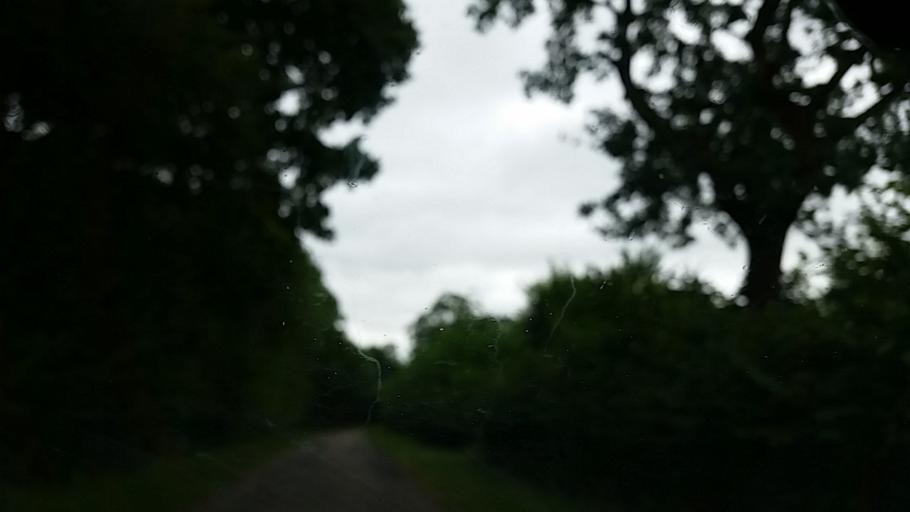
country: DE
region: Schleswig-Holstein
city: Dannewerk
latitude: 54.4981
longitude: 9.5111
